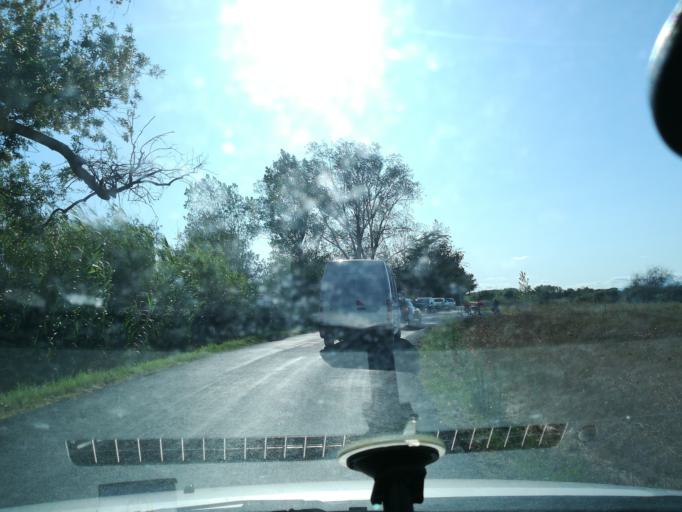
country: FR
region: Languedoc-Roussillon
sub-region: Departement de l'Herault
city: Vias
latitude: 43.2909
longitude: 3.3900
